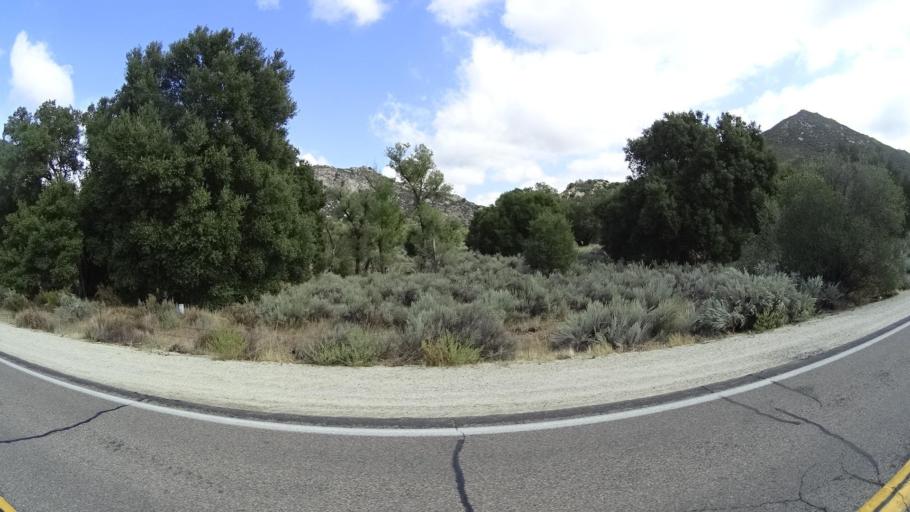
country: US
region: California
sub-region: San Diego County
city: Campo
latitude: 32.7008
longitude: -116.4891
